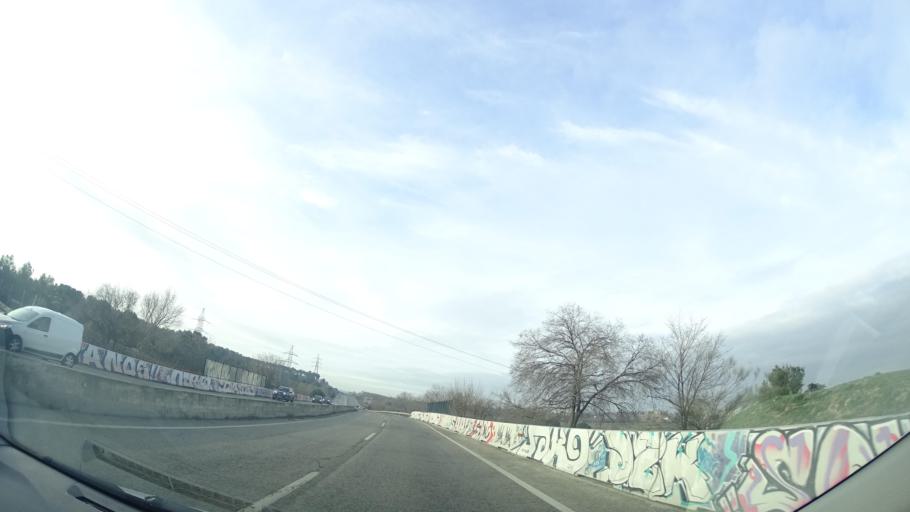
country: ES
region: Madrid
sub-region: Provincia de Madrid
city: Moncloa-Aravaca
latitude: 40.4480
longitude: -3.7668
